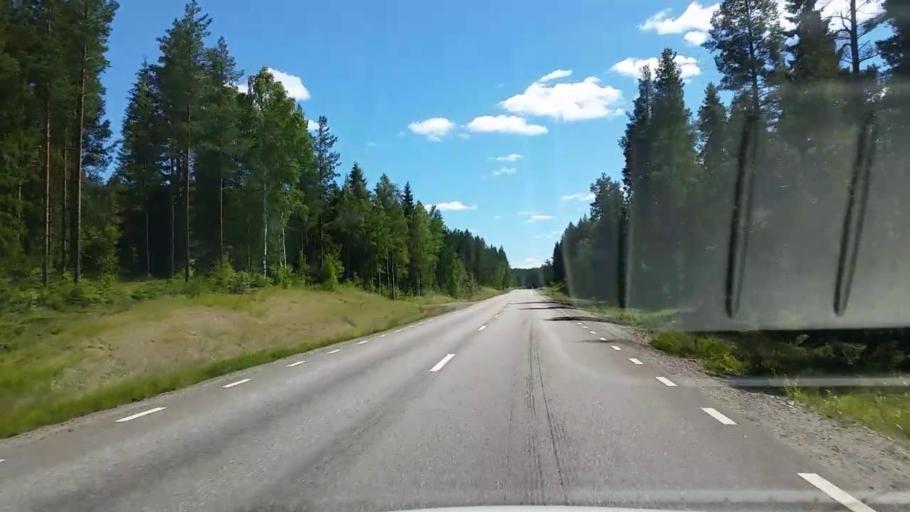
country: SE
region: Gaevleborg
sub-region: Ovanakers Kommun
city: Edsbyn
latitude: 61.1844
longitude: 15.8776
